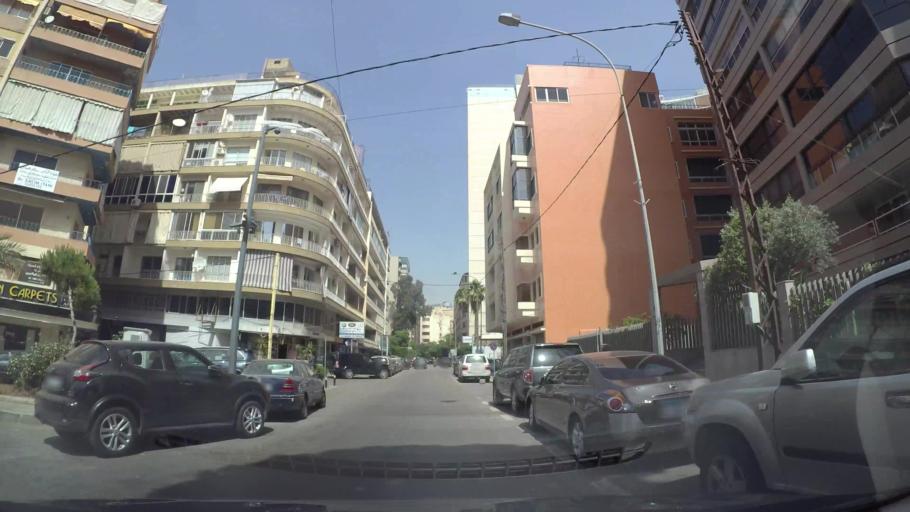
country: LB
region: Beyrouth
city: Ra's Bayrut
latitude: 33.8913
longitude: 35.4819
